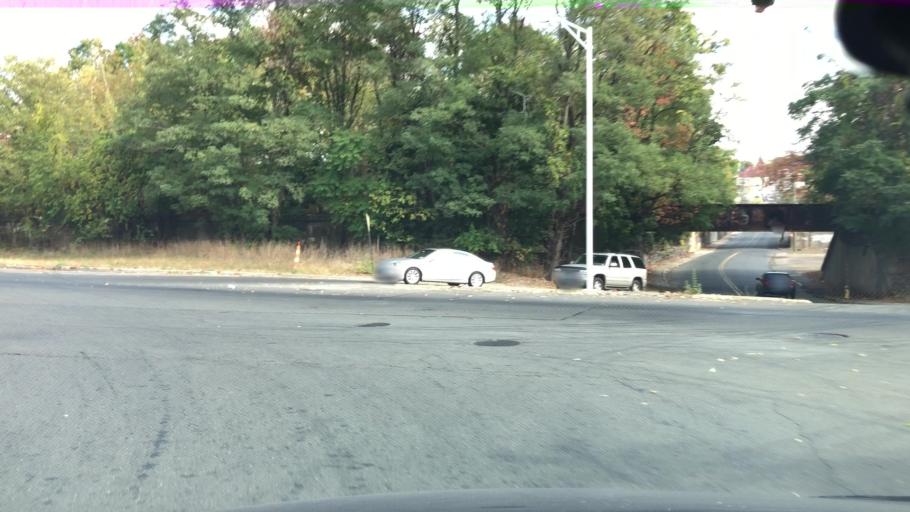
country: US
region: Connecticut
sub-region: New Haven County
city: Waterbury
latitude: 41.5441
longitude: -73.0443
